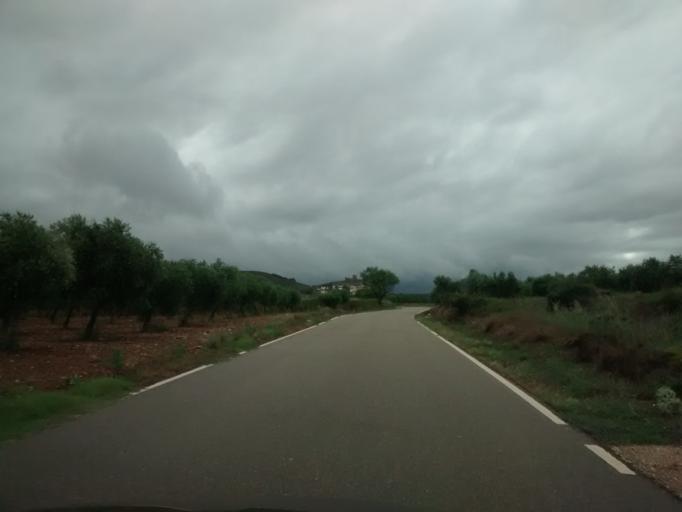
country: ES
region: Aragon
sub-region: Provincia de Zaragoza
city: Vera de Moncayo
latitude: 41.8274
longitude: -1.7030
